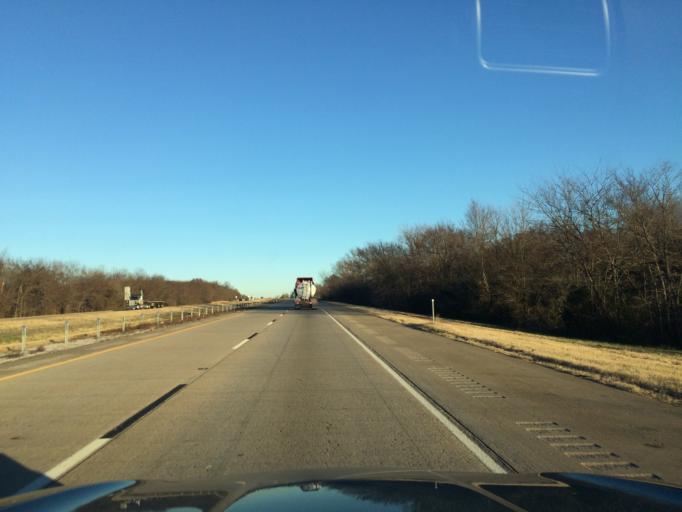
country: US
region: Oklahoma
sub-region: Sequoyah County
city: Vian
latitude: 35.4546
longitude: -94.8994
